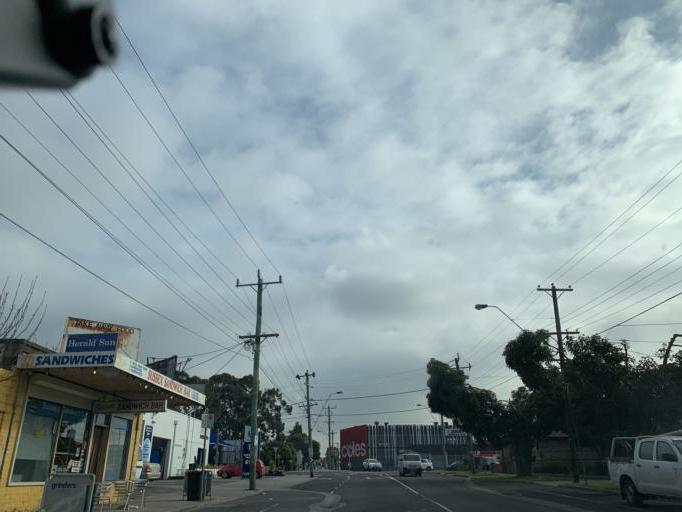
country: AU
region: Victoria
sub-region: Moreland
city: Pascoe Vale South
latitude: -37.7334
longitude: 144.9495
